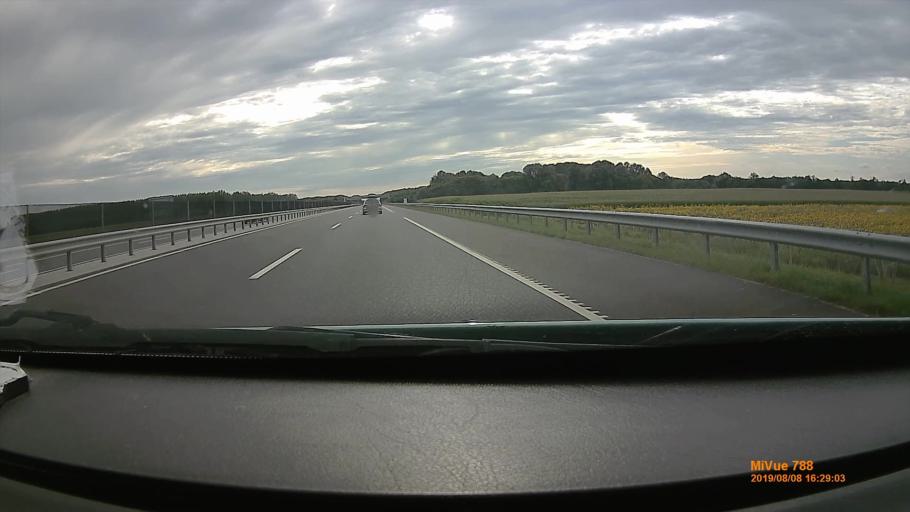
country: HU
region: Szabolcs-Szatmar-Bereg
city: Kantorjanosi
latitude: 47.9547
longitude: 22.1535
